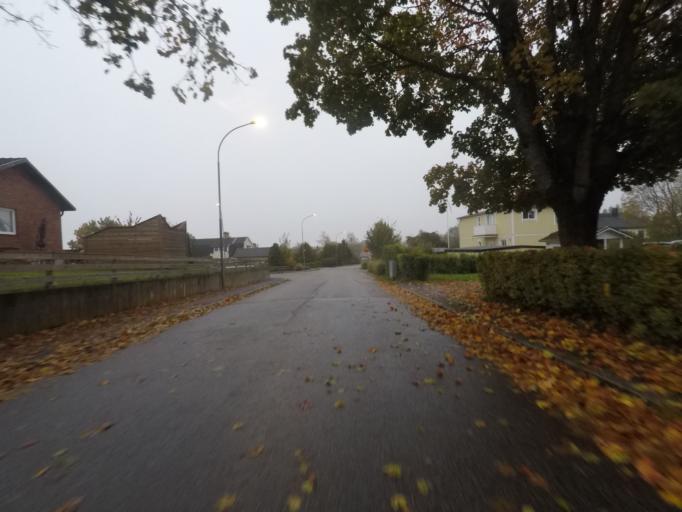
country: SE
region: OErebro
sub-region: Karlskoga Kommun
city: Karlskoga
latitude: 59.3109
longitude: 14.5067
